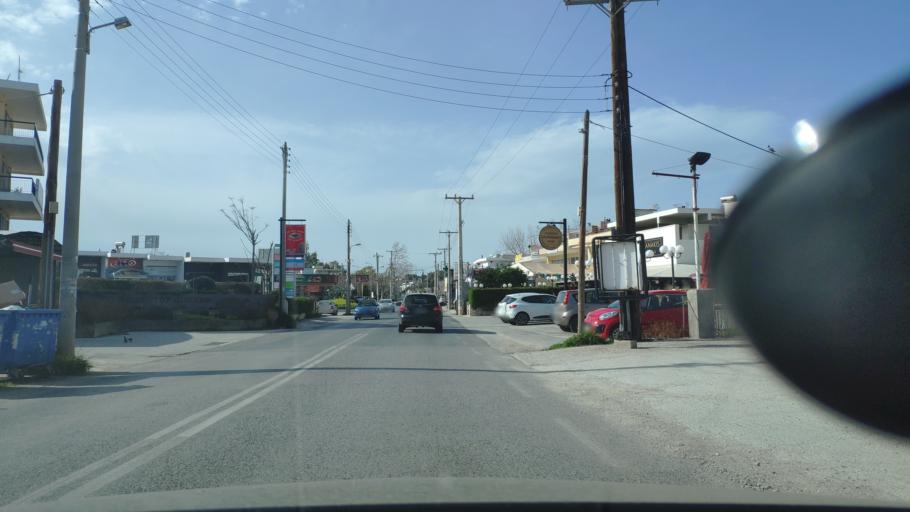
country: GR
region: Attica
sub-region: Nomarchia Anatolikis Attikis
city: Limin Mesoyaias
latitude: 37.8855
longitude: 24.0062
